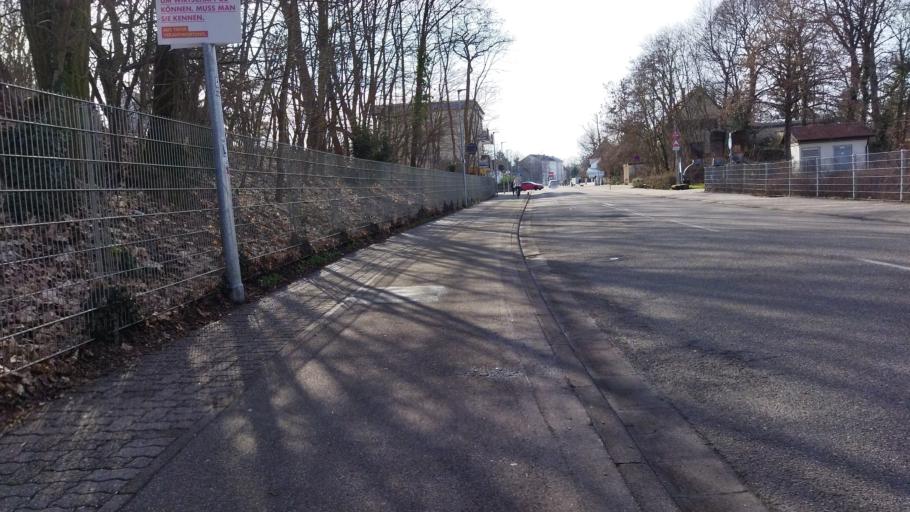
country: DE
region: Rheinland-Pfalz
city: Germersheim
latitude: 49.2163
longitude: 8.3687
